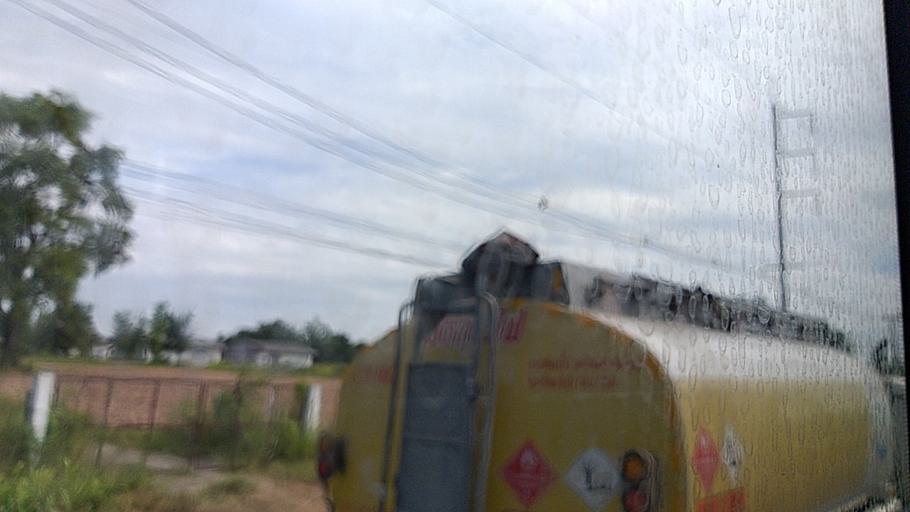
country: TH
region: Maha Sarakham
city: Chiang Yuen
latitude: 16.4331
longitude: 103.0565
